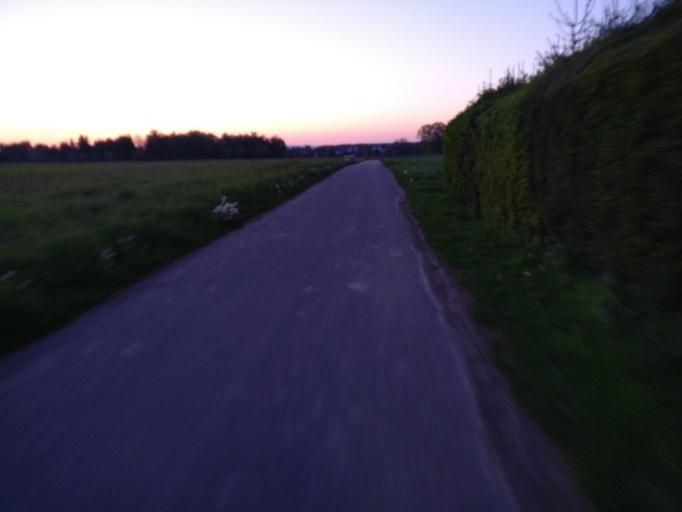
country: DE
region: Rheinland-Pfalz
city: Holzheim
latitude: 50.3620
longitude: 8.0926
